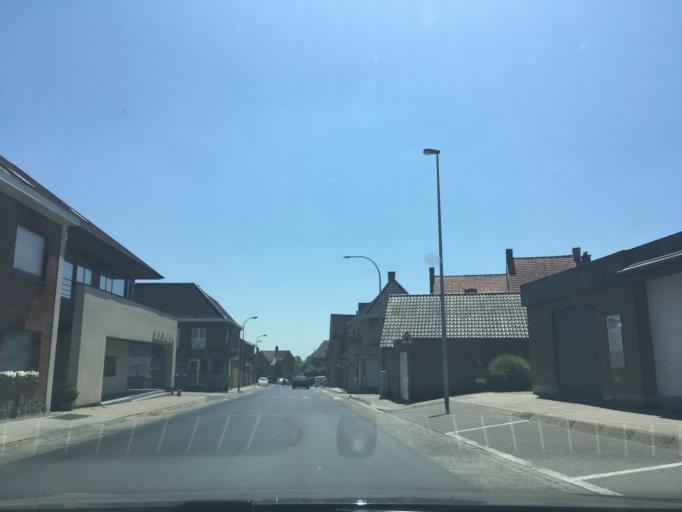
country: BE
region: Flanders
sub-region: Provincie West-Vlaanderen
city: Ardooie
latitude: 51.0032
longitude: 3.2104
